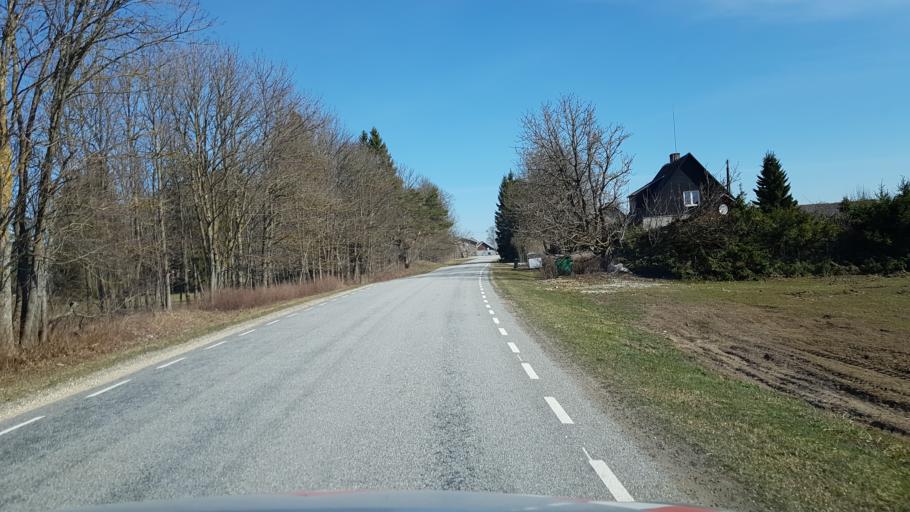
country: EE
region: Laeaene-Virumaa
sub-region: Vinni vald
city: Vinni
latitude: 59.2649
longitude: 26.3645
